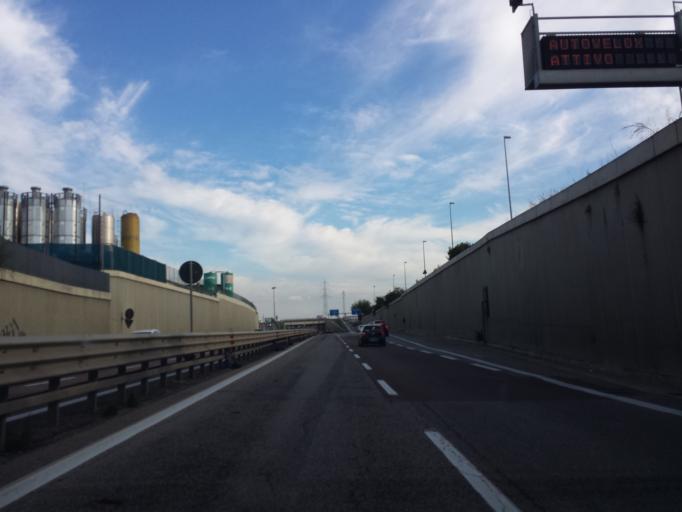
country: IT
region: Veneto
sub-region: Provincia di Verona
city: San Giovanni Lupatoto
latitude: 45.3947
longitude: 11.0170
